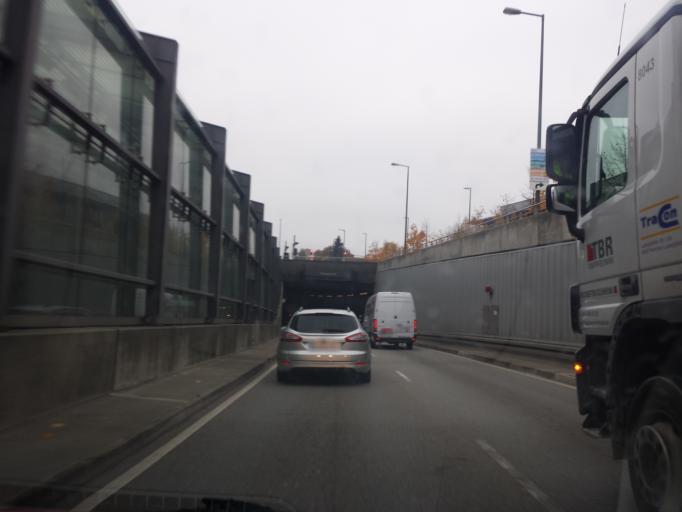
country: DE
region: Bavaria
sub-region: Upper Bavaria
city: Bogenhausen
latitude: 48.1775
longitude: 11.5873
